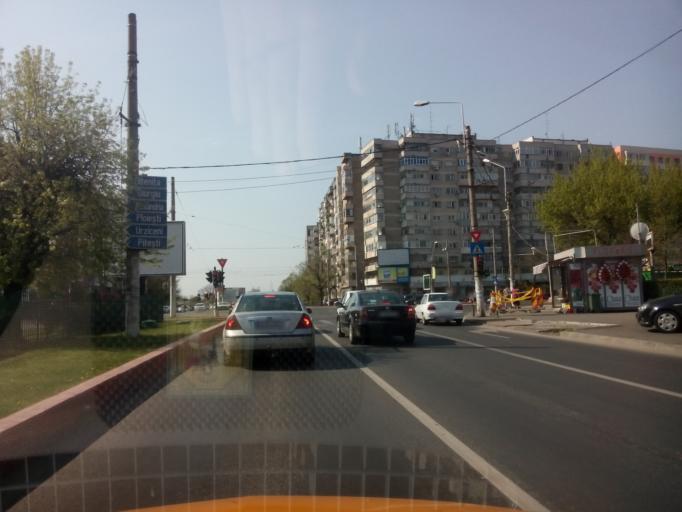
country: RO
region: Ilfov
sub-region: Comuna Popesti-Leordeni
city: Popesti-Leordeni
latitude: 44.4137
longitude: 26.1640
